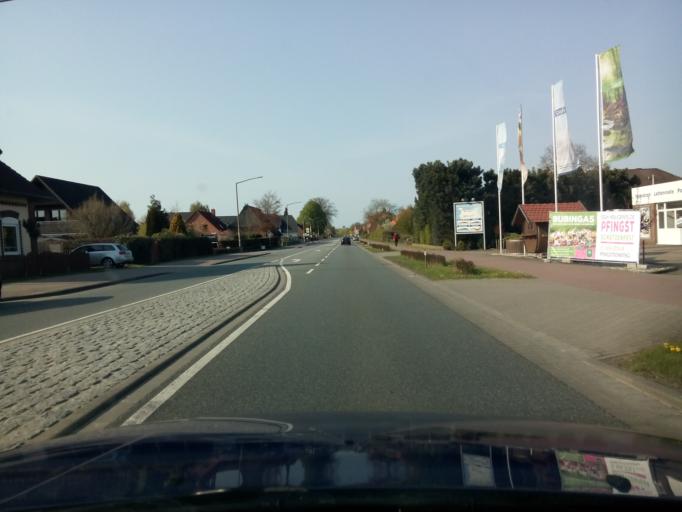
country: DE
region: Lower Saxony
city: Syke
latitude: 52.9333
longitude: 8.8252
